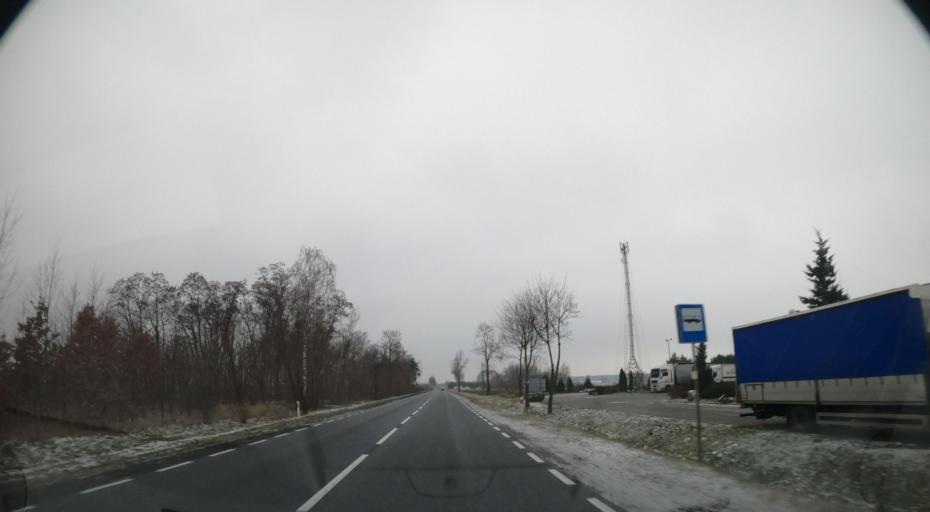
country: PL
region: Masovian Voivodeship
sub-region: Powiat plocki
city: Bodzanow
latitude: 52.4509
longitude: 20.0074
